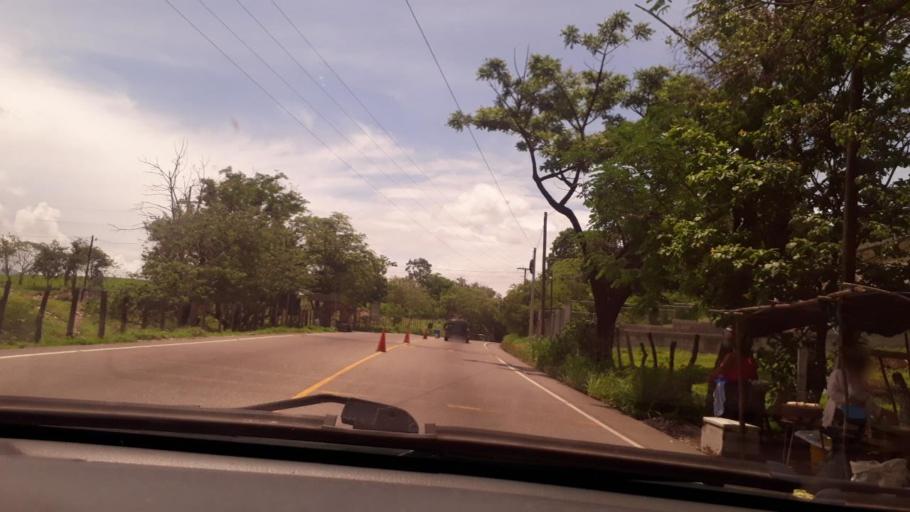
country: GT
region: Zacapa
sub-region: Municipio de Zacapa
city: Gualan
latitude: 15.0940
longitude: -89.4355
